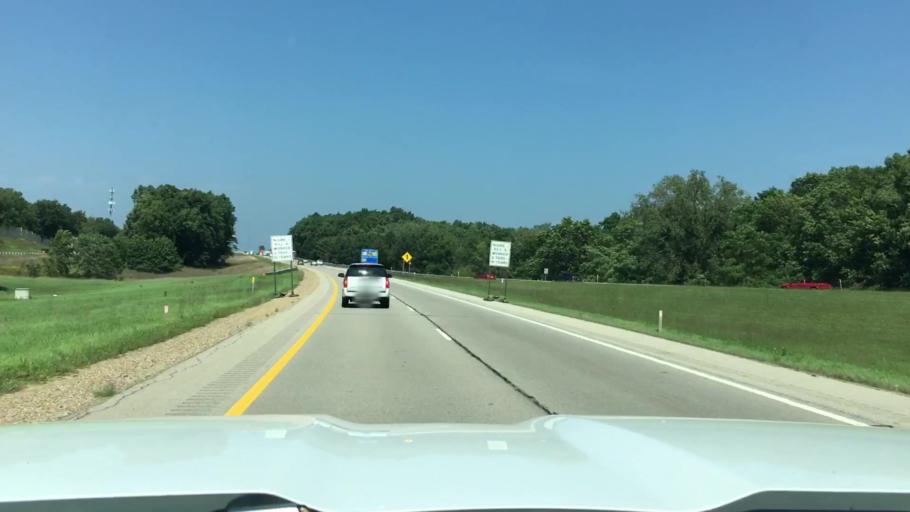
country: US
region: Michigan
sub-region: Kalamazoo County
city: Westwood
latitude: 42.2397
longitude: -85.6377
